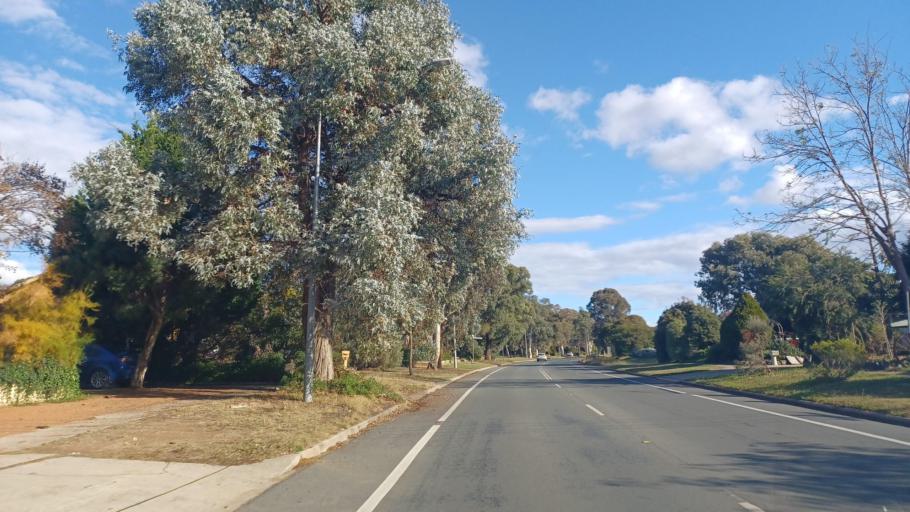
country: AU
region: Australian Capital Territory
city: Belconnen
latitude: -35.1888
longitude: 149.0475
